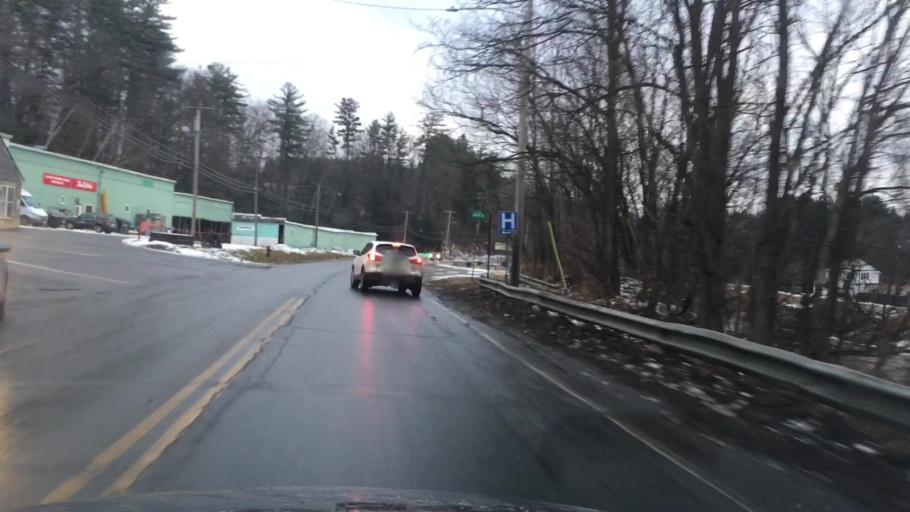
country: US
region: New Hampshire
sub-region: Sullivan County
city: Claremont
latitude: 43.3864
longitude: -72.3532
